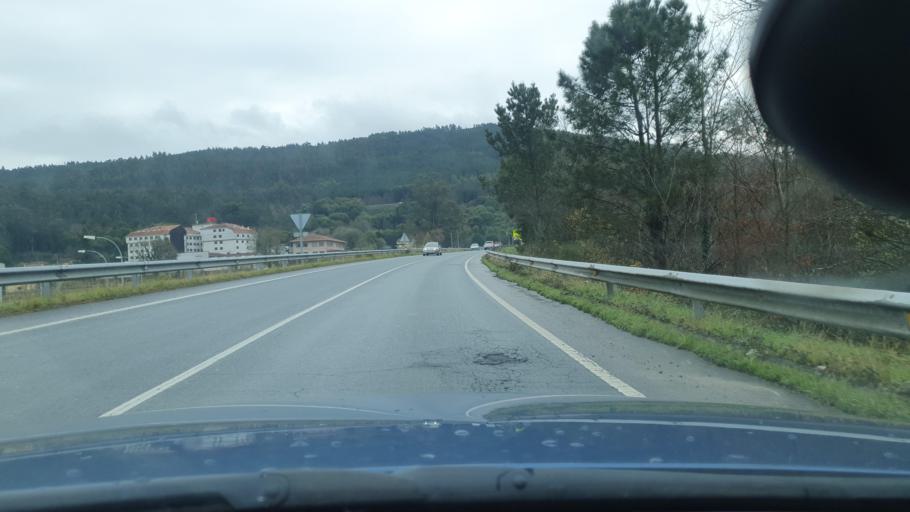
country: ES
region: Galicia
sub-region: Provincia da Coruna
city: Padron
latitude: 42.7566
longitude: -8.6565
